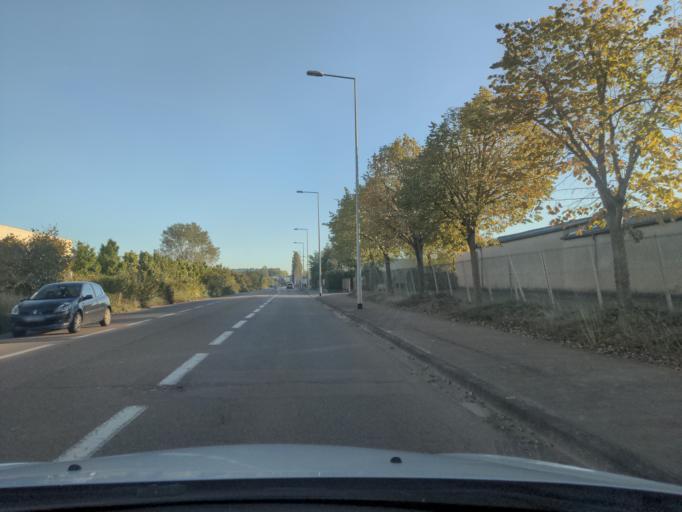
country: FR
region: Bourgogne
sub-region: Departement de la Cote-d'Or
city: Saint-Apollinaire
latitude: 47.3436
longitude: 5.0627
